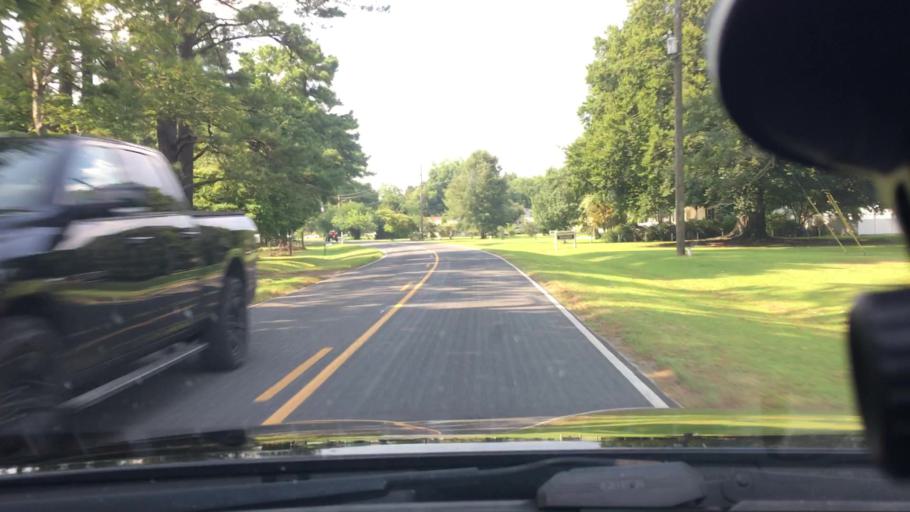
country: US
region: North Carolina
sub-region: Craven County
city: New Bern
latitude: 35.1728
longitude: -77.0512
